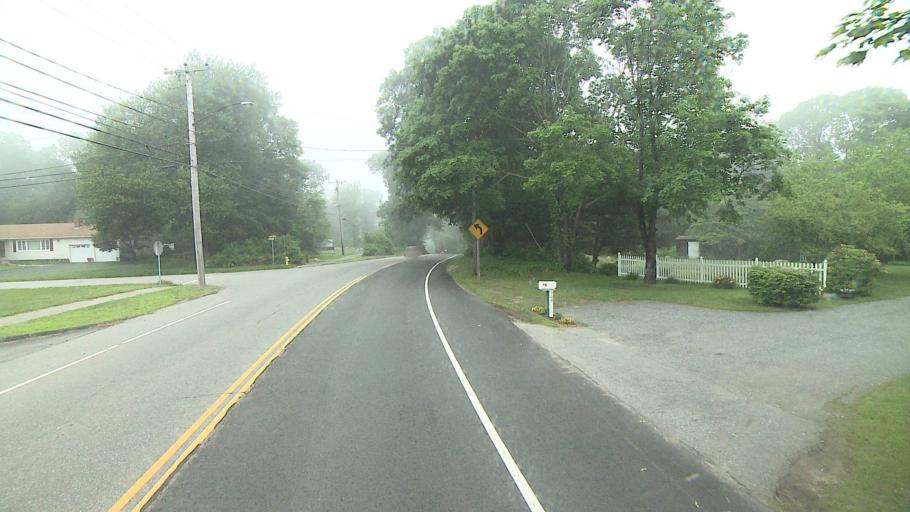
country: US
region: Connecticut
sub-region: New London County
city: Poquonock Bridge
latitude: 41.3479
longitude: -72.0112
